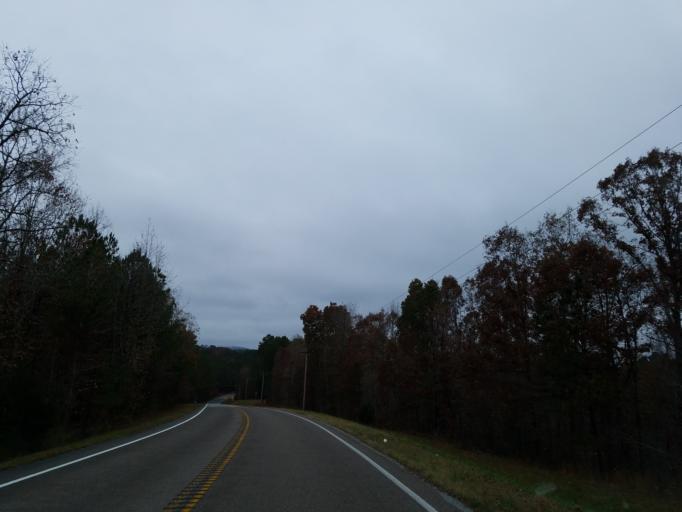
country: US
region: Georgia
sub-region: Cherokee County
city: Canton
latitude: 34.2885
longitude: -84.5550
